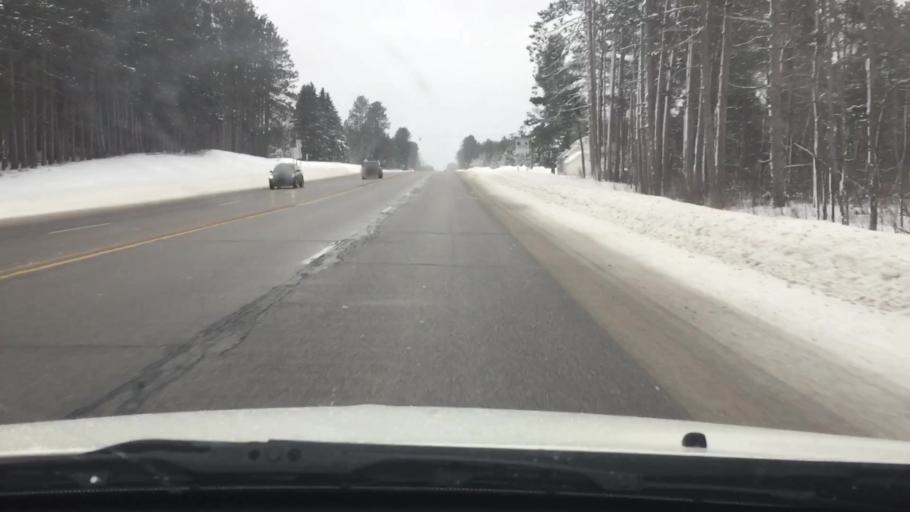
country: US
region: Michigan
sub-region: Otsego County
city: Gaylord
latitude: 45.0415
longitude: -84.7758
